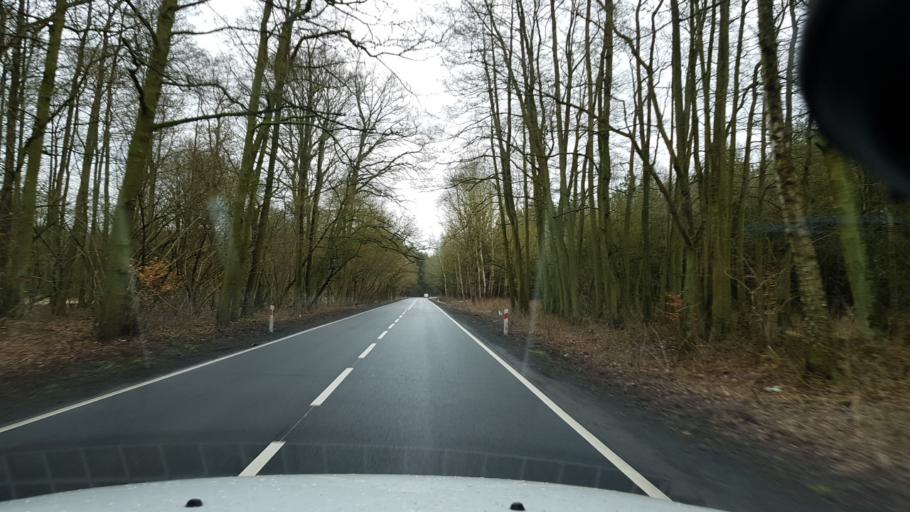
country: PL
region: West Pomeranian Voivodeship
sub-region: Powiat goleniowski
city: Stepnica
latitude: 53.6435
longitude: 14.6583
